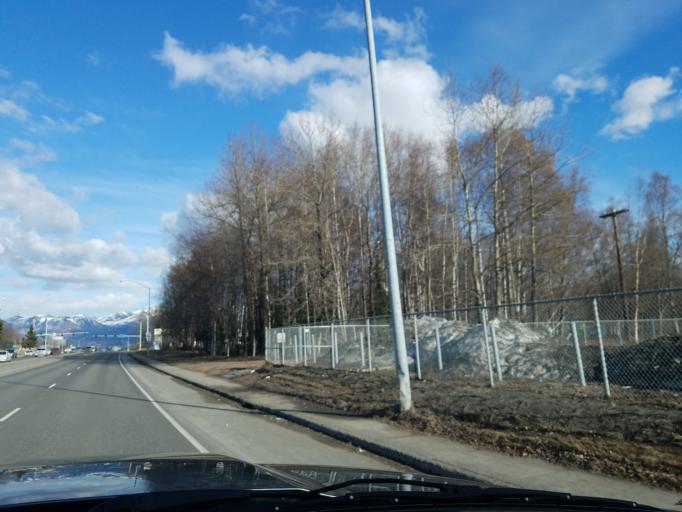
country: US
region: Alaska
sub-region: Anchorage Municipality
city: Anchorage
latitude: 61.1807
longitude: -149.9023
